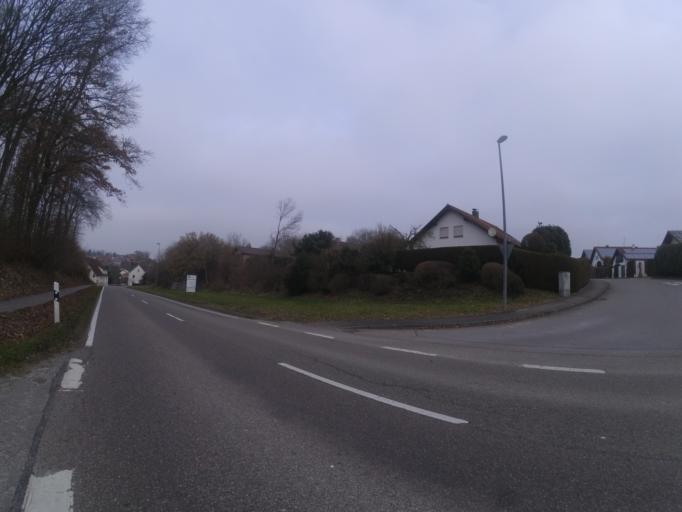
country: DE
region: Baden-Wuerttemberg
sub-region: Tuebingen Region
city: Untermarchtal
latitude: 48.2399
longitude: 9.6169
